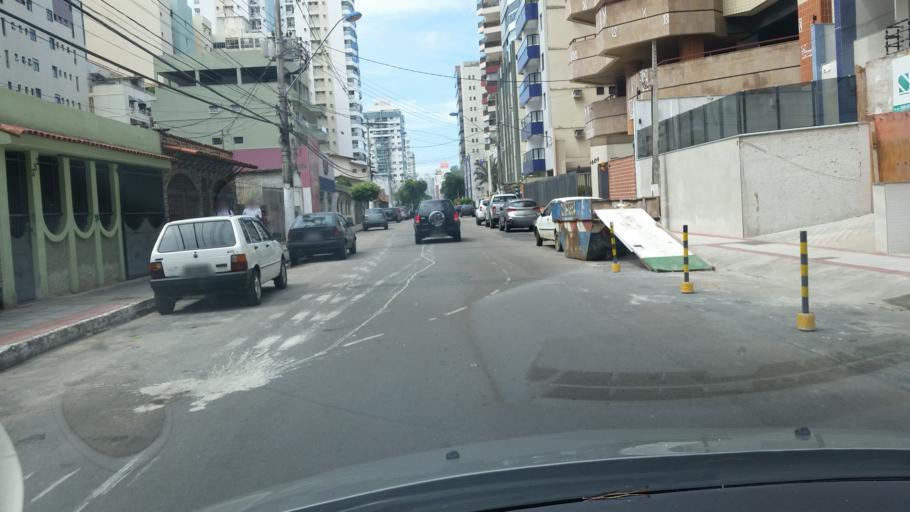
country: BR
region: Espirito Santo
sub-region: Vila Velha
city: Vila Velha
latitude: -20.3434
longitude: -40.2864
